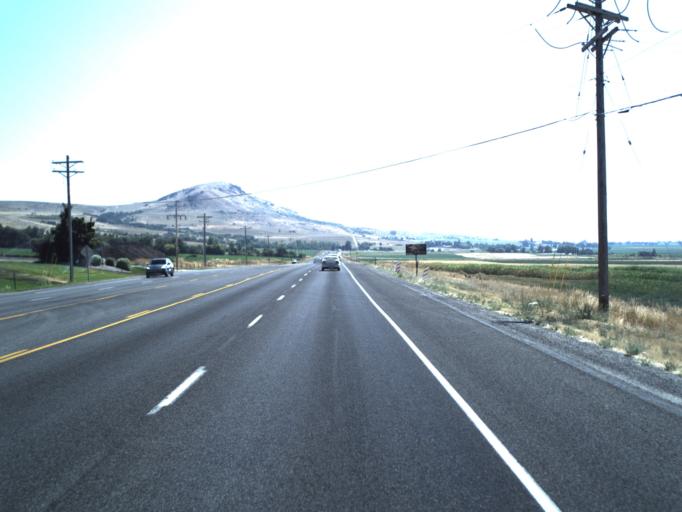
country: US
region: Utah
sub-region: Cache County
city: Richmond
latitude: 41.9072
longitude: -111.8148
